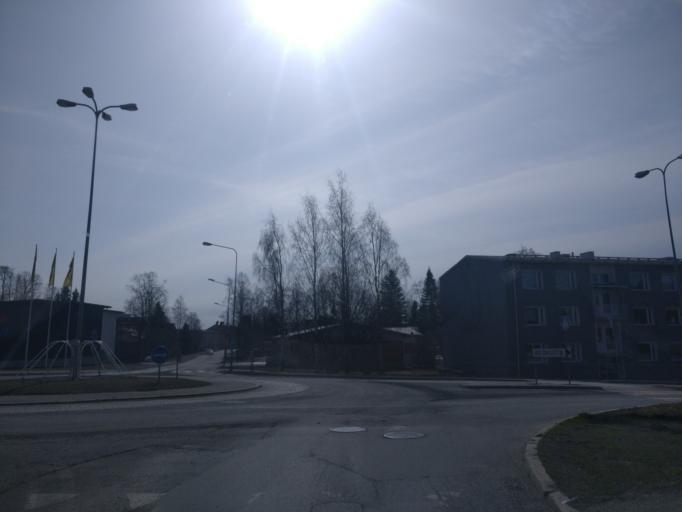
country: FI
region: Lapland
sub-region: Kemi-Tornio
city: Kemi
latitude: 65.7301
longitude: 24.5993
